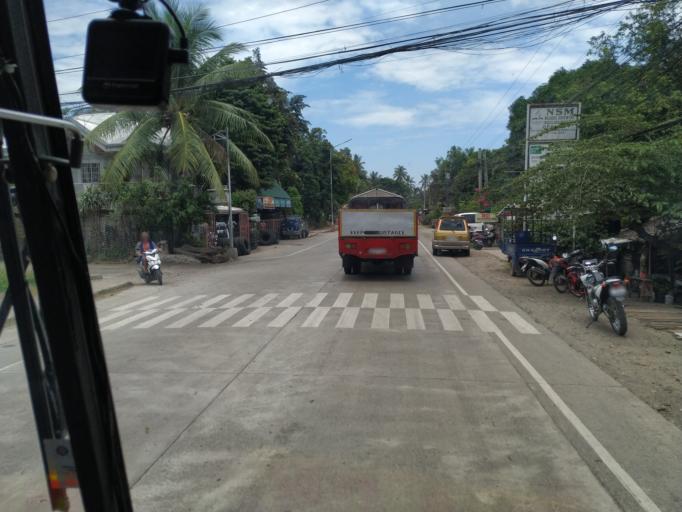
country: PH
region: Central Visayas
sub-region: Province of Negros Oriental
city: Sibulan
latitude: 9.3511
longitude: 123.2852
